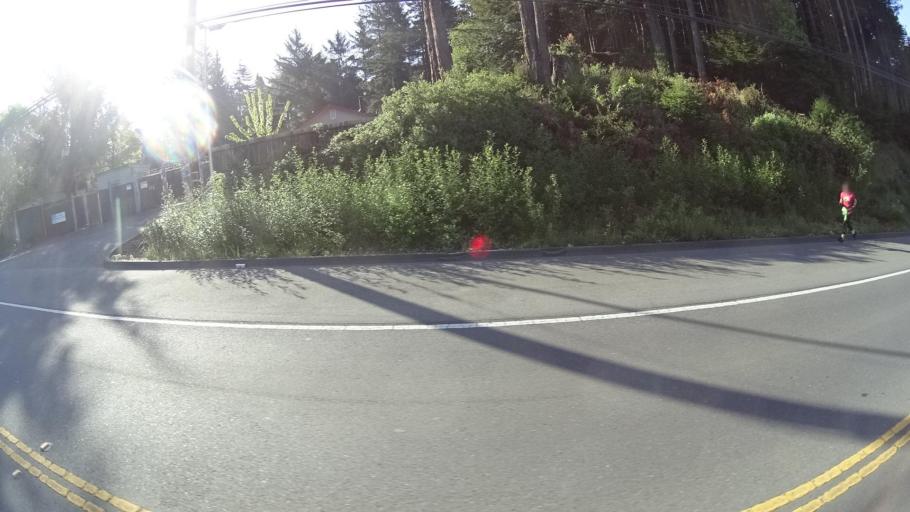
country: US
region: California
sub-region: Humboldt County
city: Bayview
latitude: 40.7705
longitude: -124.1748
